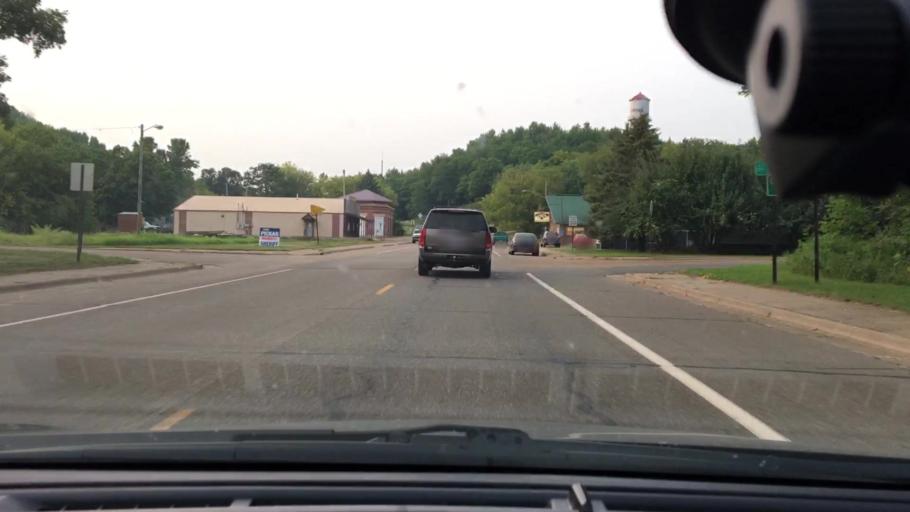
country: US
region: Minnesota
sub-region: Crow Wing County
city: Crosby
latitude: 46.5167
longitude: -93.9232
